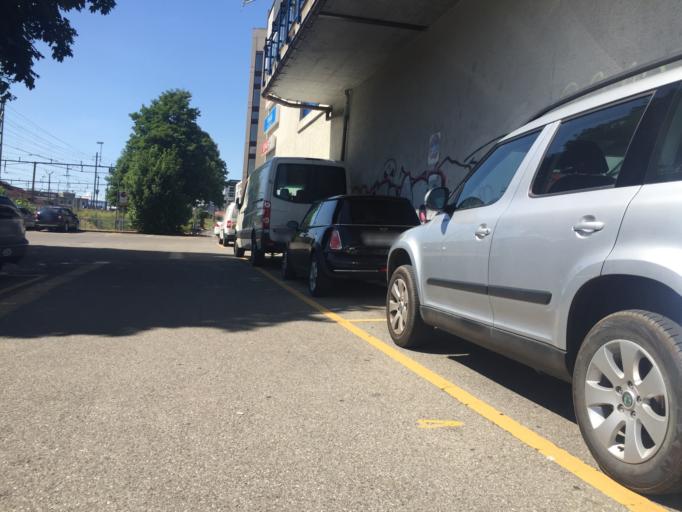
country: CH
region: Bern
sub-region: Thun District
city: Thun
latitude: 46.7572
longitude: 7.6266
